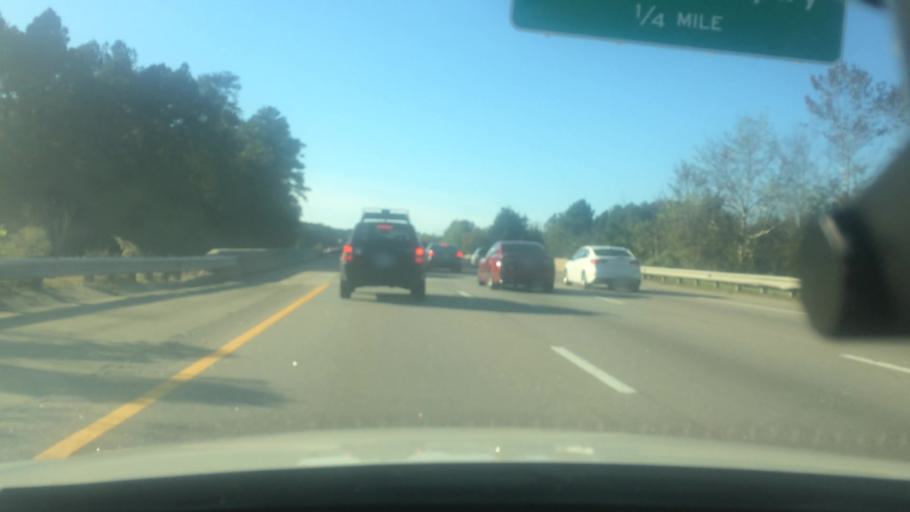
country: US
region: North Carolina
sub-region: Wake County
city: Morrisville
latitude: 35.8995
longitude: -78.8705
